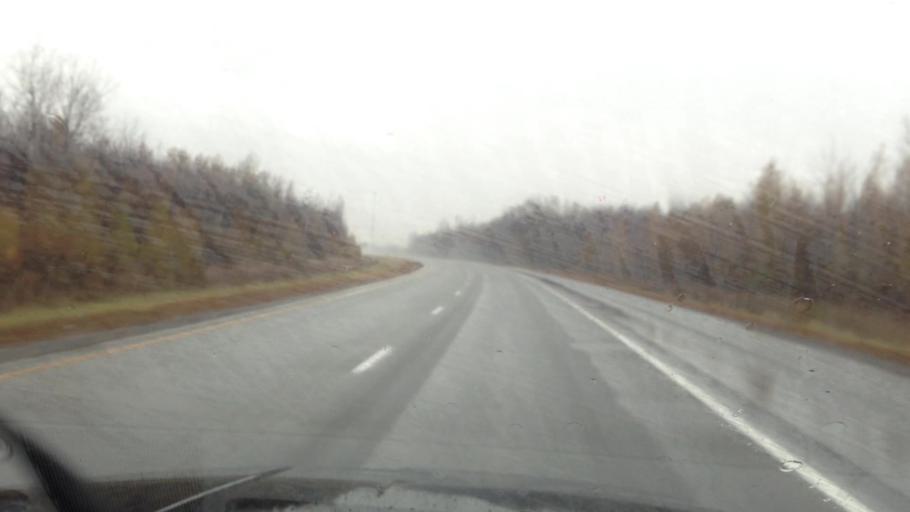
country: CA
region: Ontario
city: Casselman
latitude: 45.3047
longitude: -75.1438
